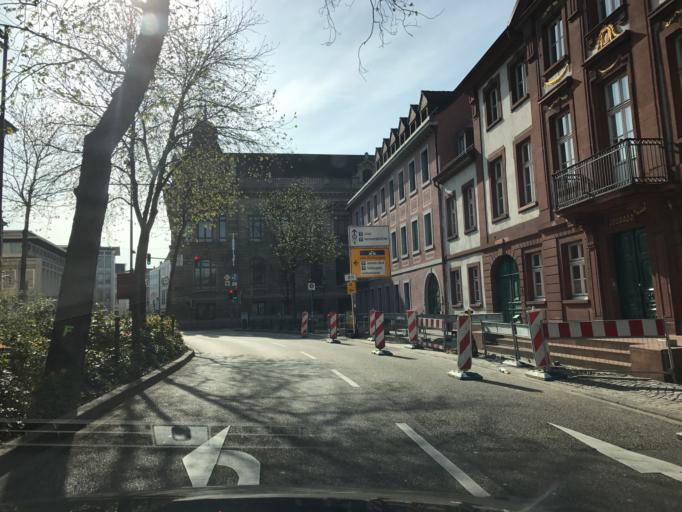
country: DE
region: Baden-Wuerttemberg
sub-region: Karlsruhe Region
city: Karlsruhe
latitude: 49.0118
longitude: 8.3993
